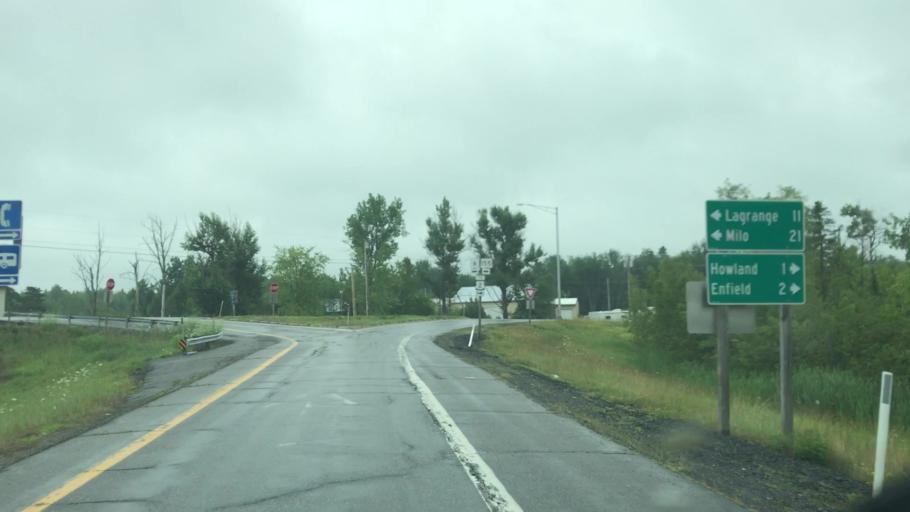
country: US
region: Maine
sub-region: Penobscot County
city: Howland
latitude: 45.2359
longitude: -68.6754
